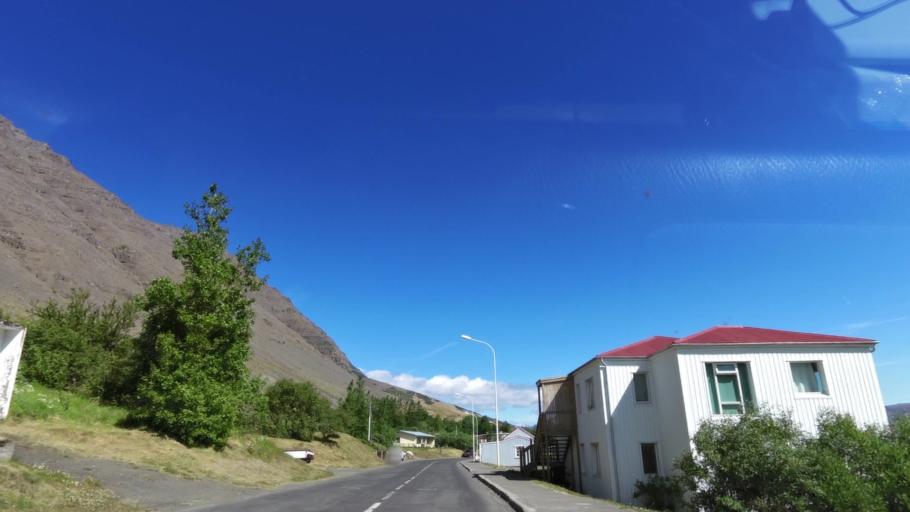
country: IS
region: Westfjords
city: Isafjoerdur
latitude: 65.6818
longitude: -23.6088
